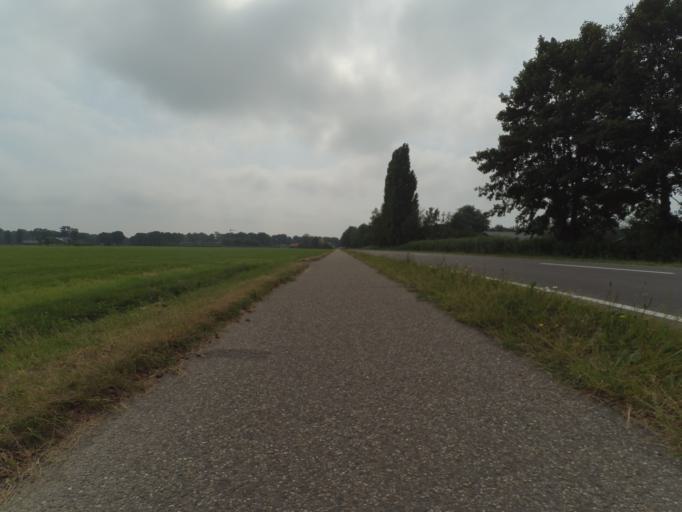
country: NL
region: Gelderland
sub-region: Gemeente Ede
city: Lunteren
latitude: 52.1003
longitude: 5.6103
